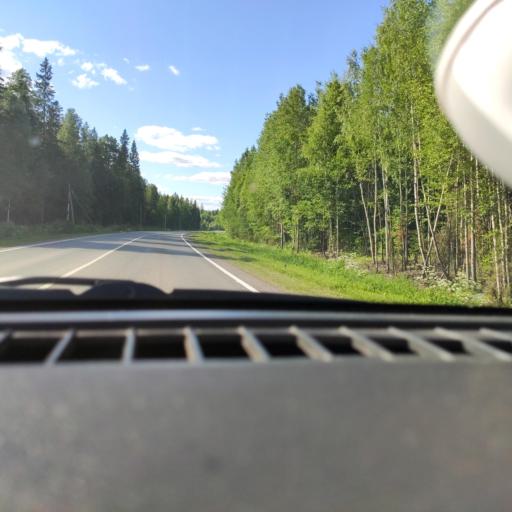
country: RU
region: Perm
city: Perm
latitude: 58.2166
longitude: 56.1728
